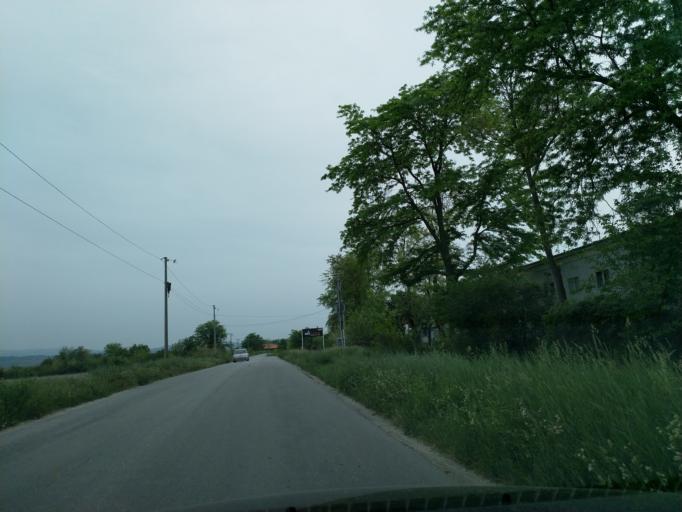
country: RS
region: Central Serbia
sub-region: Pomoravski Okrug
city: Jagodina
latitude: 43.9721
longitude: 21.2370
